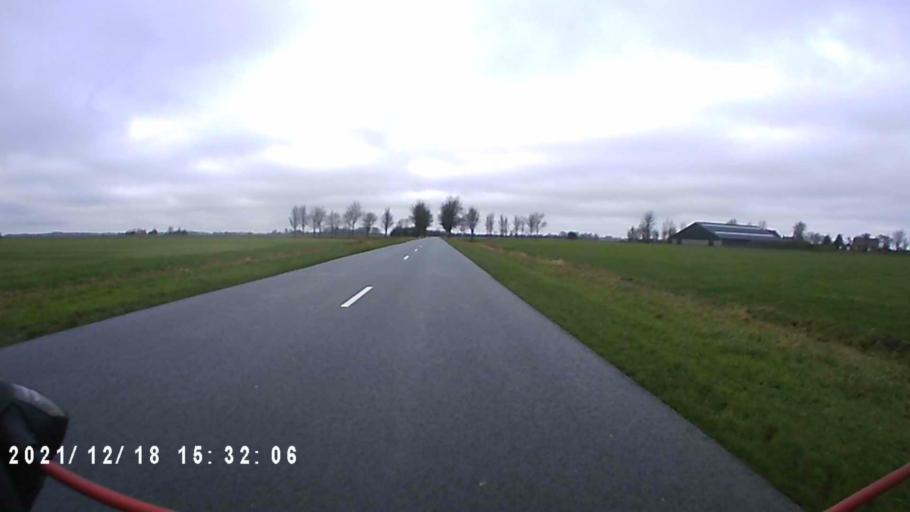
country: NL
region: Friesland
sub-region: Gemeente Dongeradeel
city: Anjum
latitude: 53.3411
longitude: 6.1354
